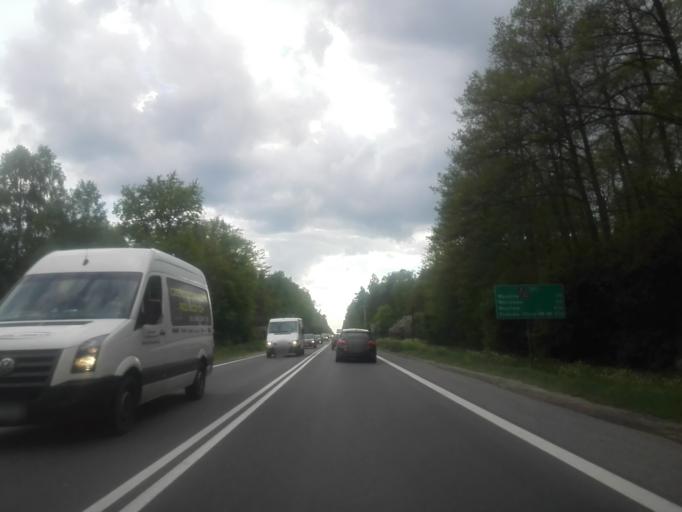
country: PL
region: Masovian Voivodeship
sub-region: Powiat ostrowski
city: Ostrow Mazowiecka
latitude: 52.7804
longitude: 21.8495
